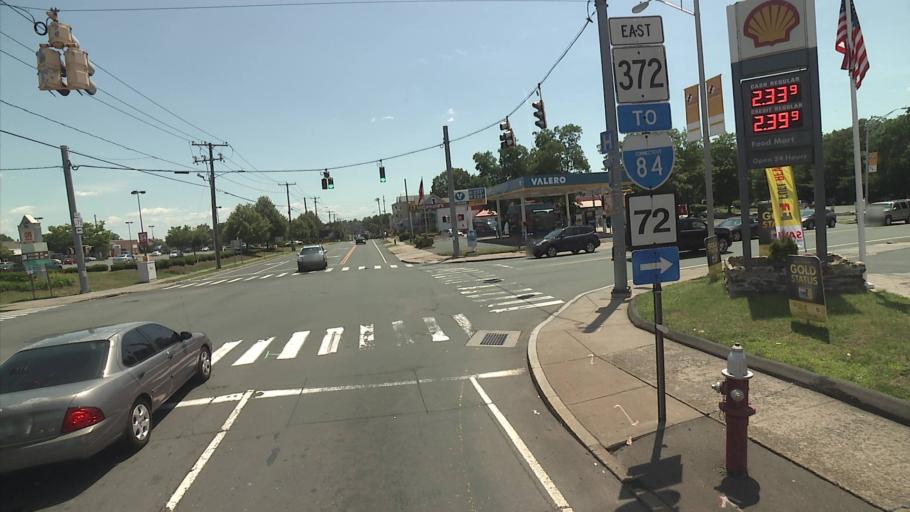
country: US
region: Connecticut
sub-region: Hartford County
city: New Britain
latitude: 41.6664
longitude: -72.8069
